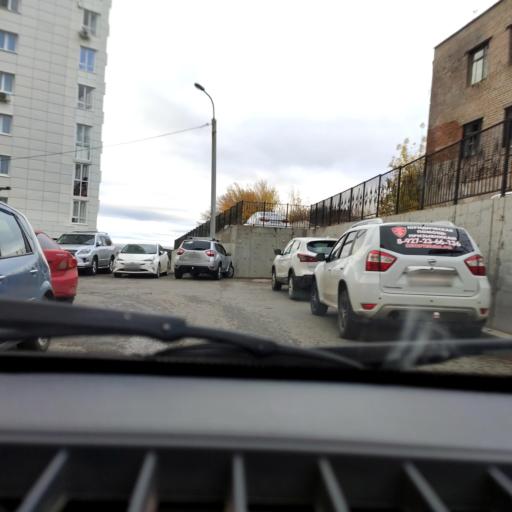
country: RU
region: Bashkortostan
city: Ufa
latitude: 54.6988
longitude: 55.9799
